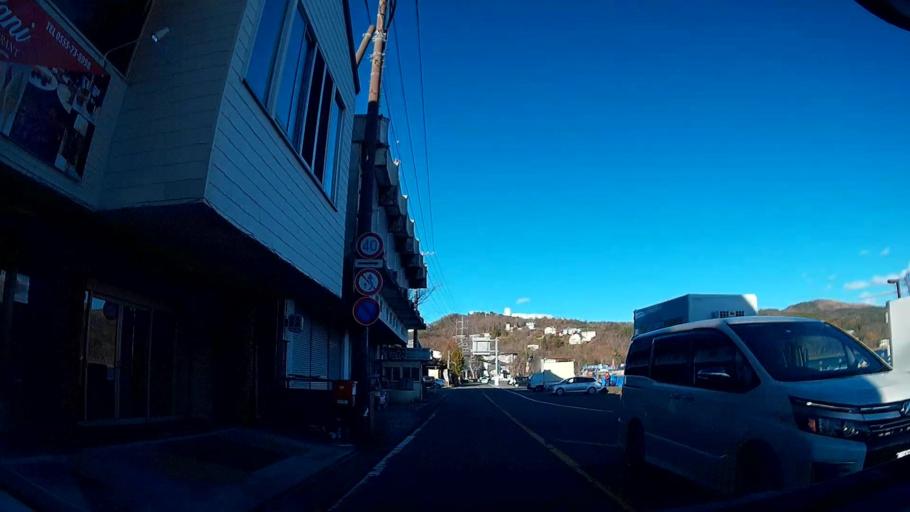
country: JP
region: Shizuoka
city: Gotemba
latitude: 35.4258
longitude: 138.8495
